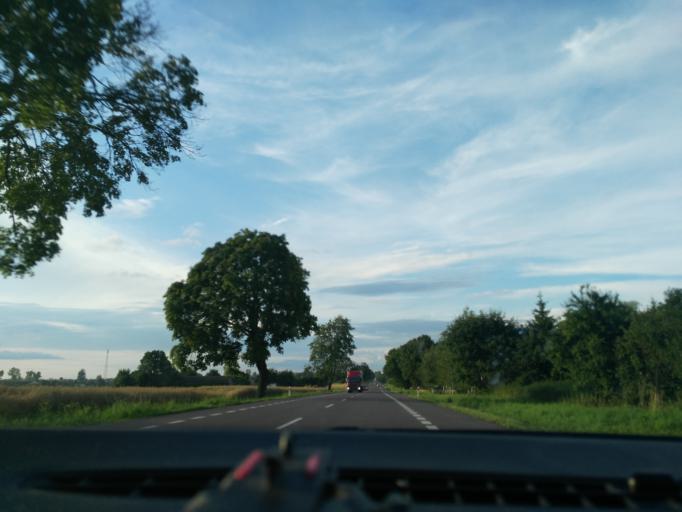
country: PL
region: Lublin Voivodeship
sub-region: Powiat krasnicki
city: Wilkolaz
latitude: 51.0469
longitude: 22.3805
